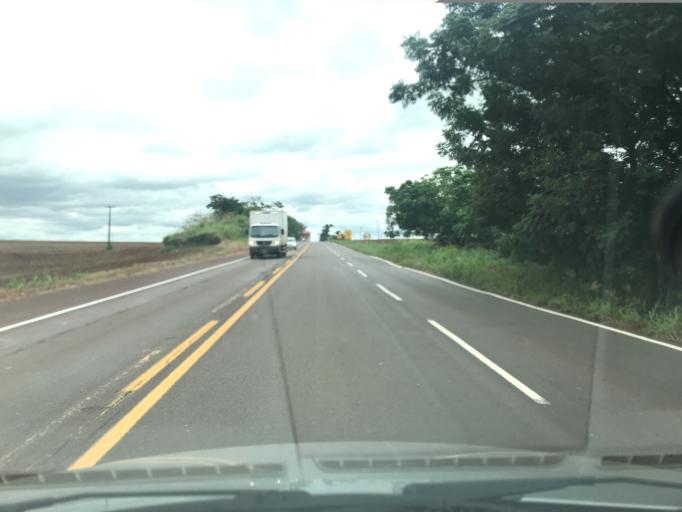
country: BR
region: Parana
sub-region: Terra Boa
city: Terra Boa
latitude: -23.5998
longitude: -52.3668
